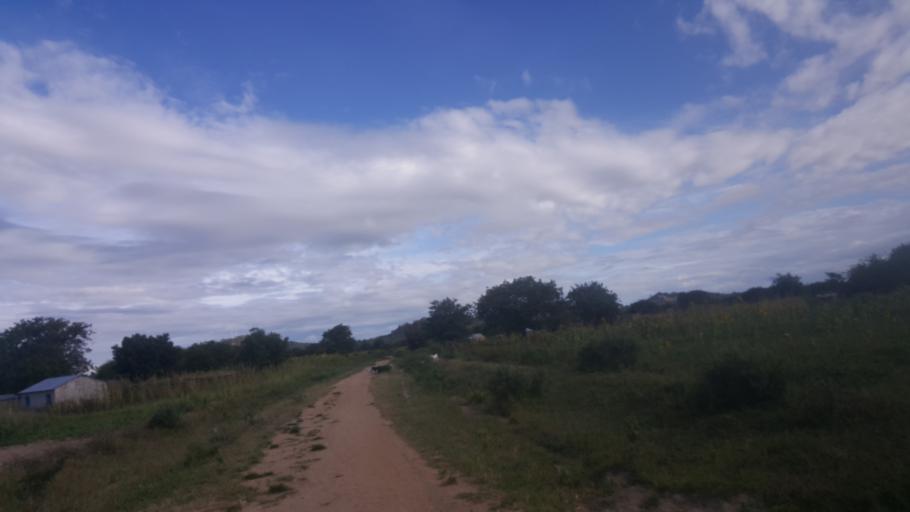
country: TZ
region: Dodoma
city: Dodoma
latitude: -6.0895
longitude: 35.5254
